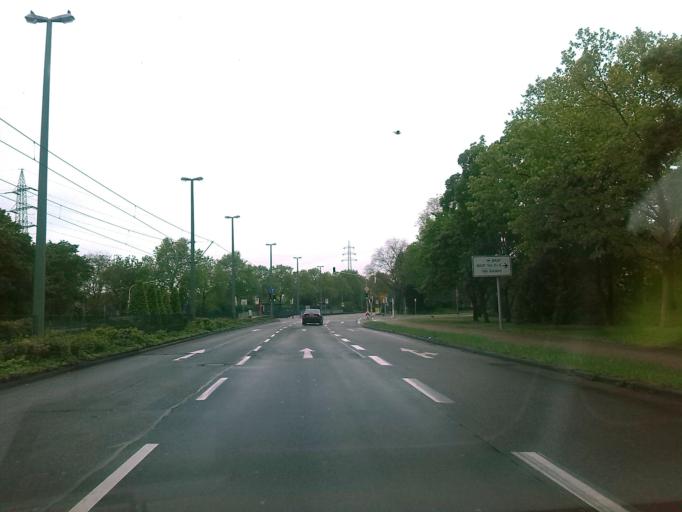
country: DE
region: Rheinland-Pfalz
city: Ludwigshafen am Rhein
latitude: 49.5043
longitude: 8.4118
